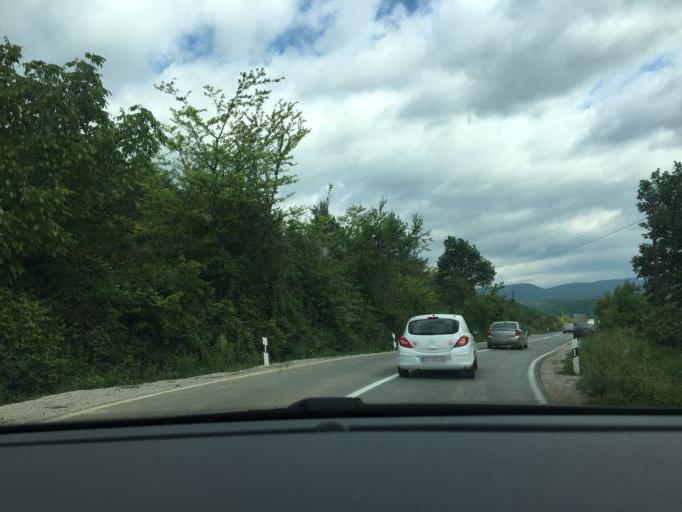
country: MK
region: Resen
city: Jankovec
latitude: 41.1147
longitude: 21.0119
